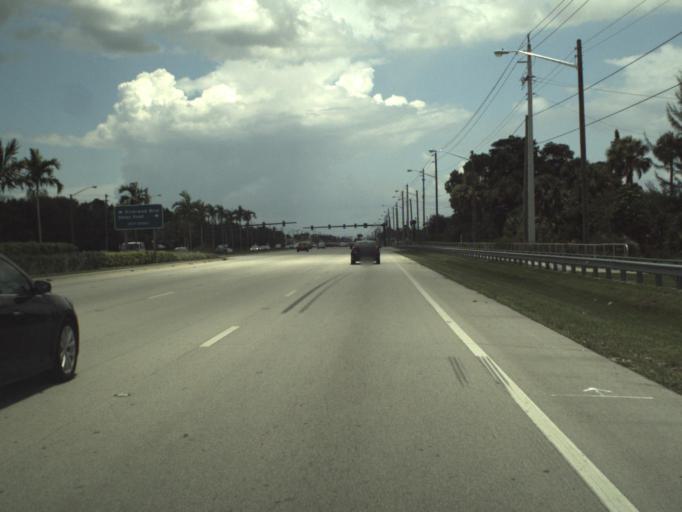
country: US
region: Florida
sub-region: Palm Beach County
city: Plantation Mobile Home Park
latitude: 26.7081
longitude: -80.1606
